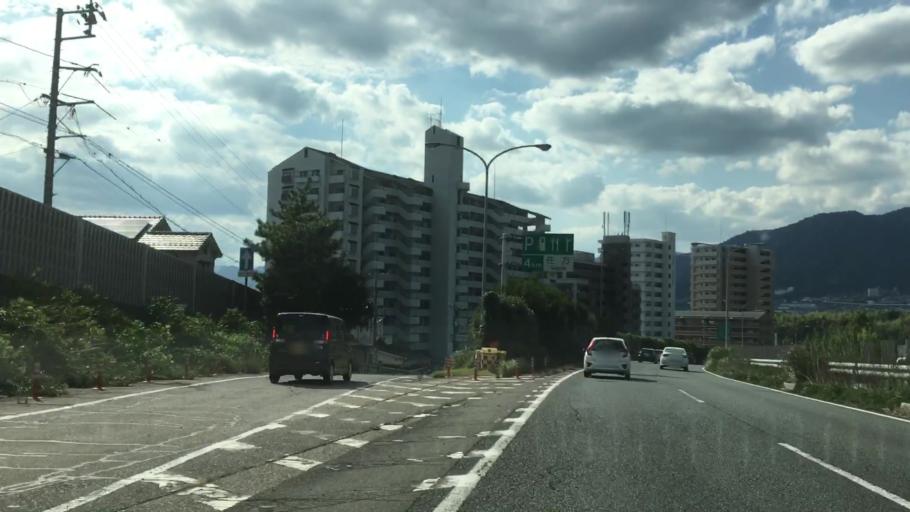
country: JP
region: Hiroshima
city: Hatsukaichi
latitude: 34.3765
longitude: 132.3707
